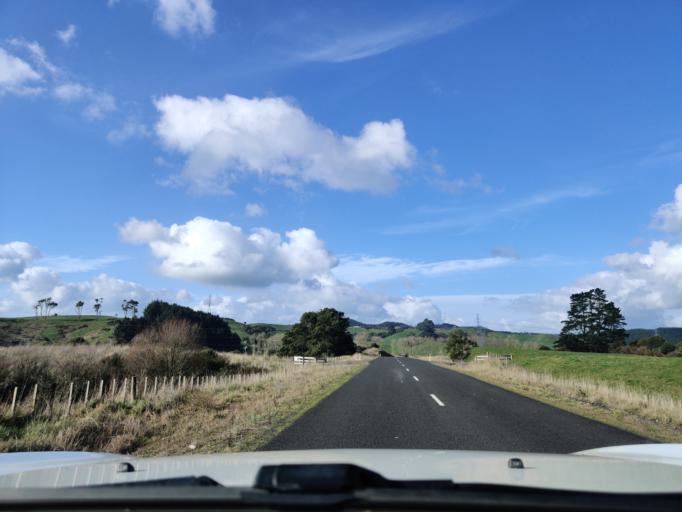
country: NZ
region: Waikato
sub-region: Waikato District
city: Te Kauwhata
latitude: -37.2830
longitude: 175.2041
